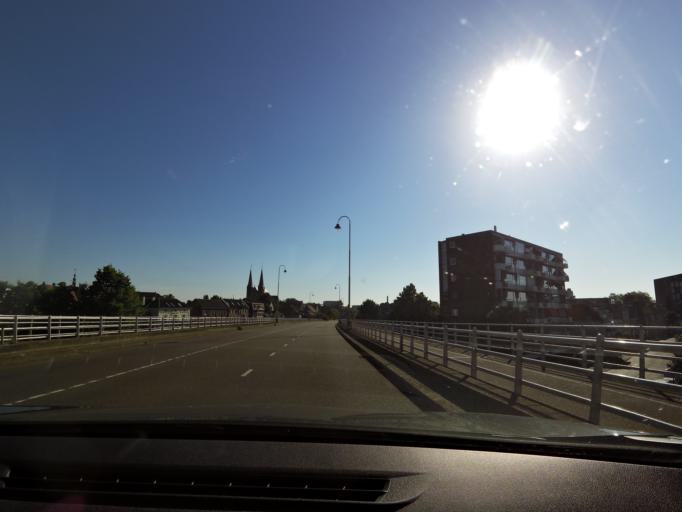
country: NL
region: Overijssel
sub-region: Gemeente Deventer
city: Deventer
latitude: 52.2494
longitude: 6.1587
